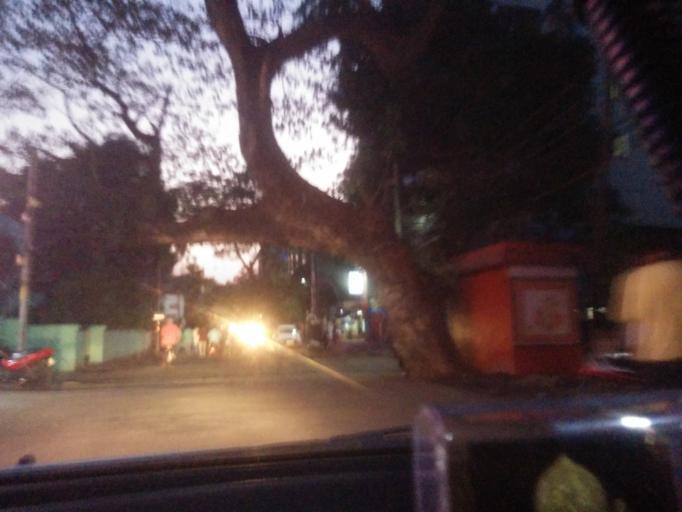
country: IN
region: Andhra Pradesh
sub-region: East Godavari
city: Rajahmundry
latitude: 17.0078
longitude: 81.7851
